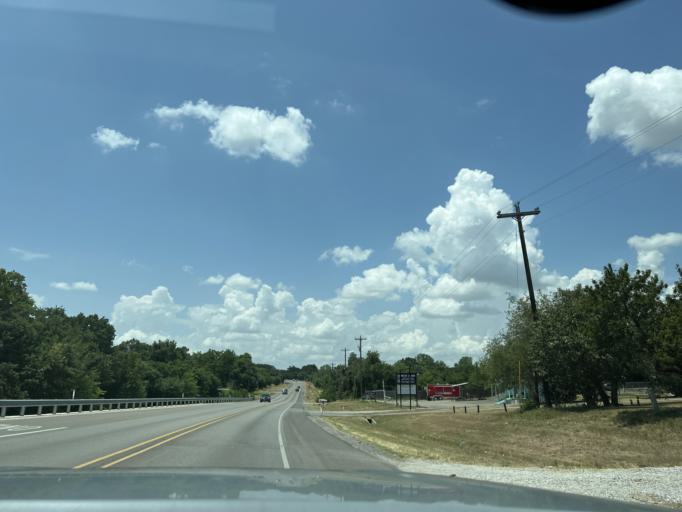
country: US
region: Texas
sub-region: Parker County
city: Weatherford
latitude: 32.7946
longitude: -97.7897
